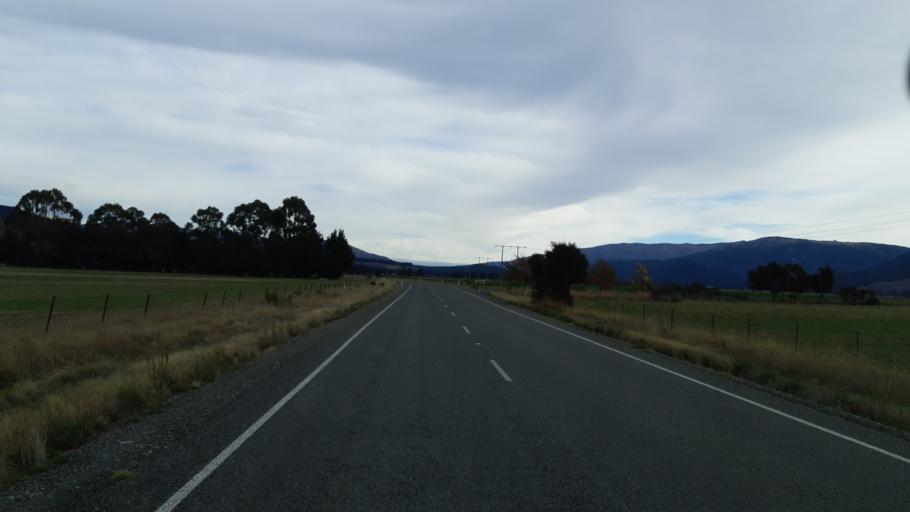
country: NZ
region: Tasman
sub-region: Tasman District
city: Brightwater
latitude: -41.6431
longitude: 173.3020
